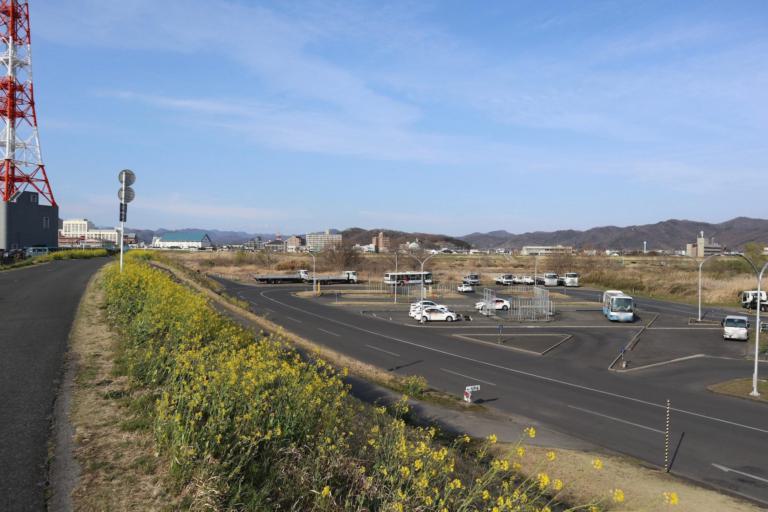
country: JP
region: Tochigi
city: Ashikaga
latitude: 36.3254
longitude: 139.4534
